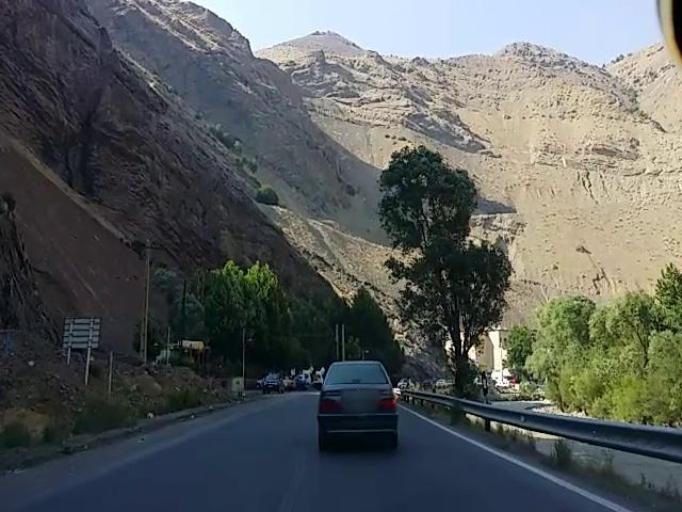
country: IR
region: Tehran
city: Tajrish
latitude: 36.0297
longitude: 51.2288
